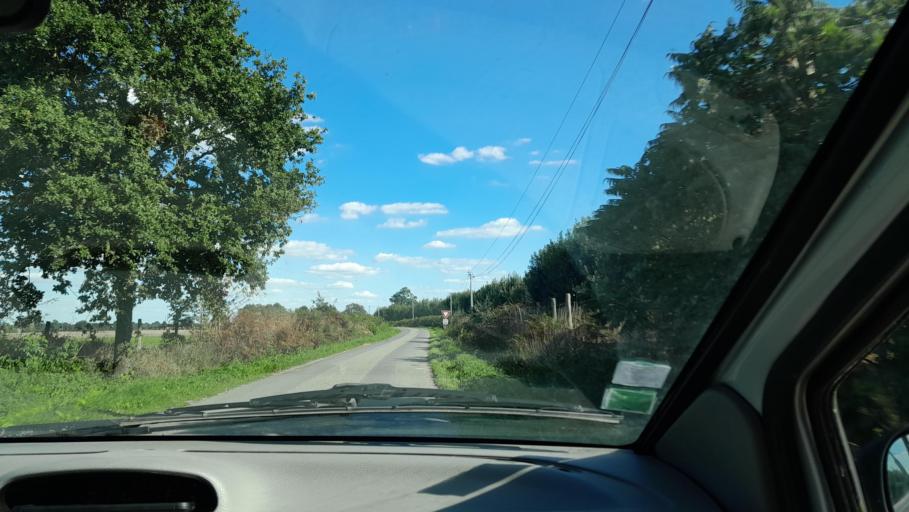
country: FR
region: Pays de la Loire
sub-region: Departement de la Mayenne
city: Ballots
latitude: 47.9541
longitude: -1.0687
